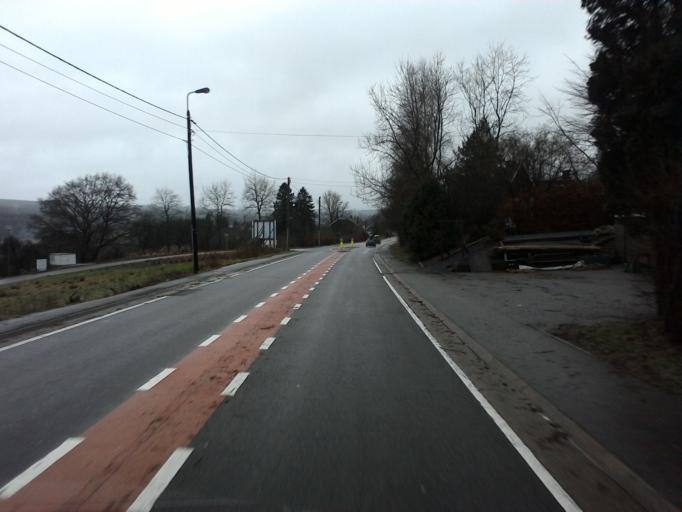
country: BE
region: Wallonia
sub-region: Province de Liege
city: Stavelot
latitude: 50.4497
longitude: 5.9458
